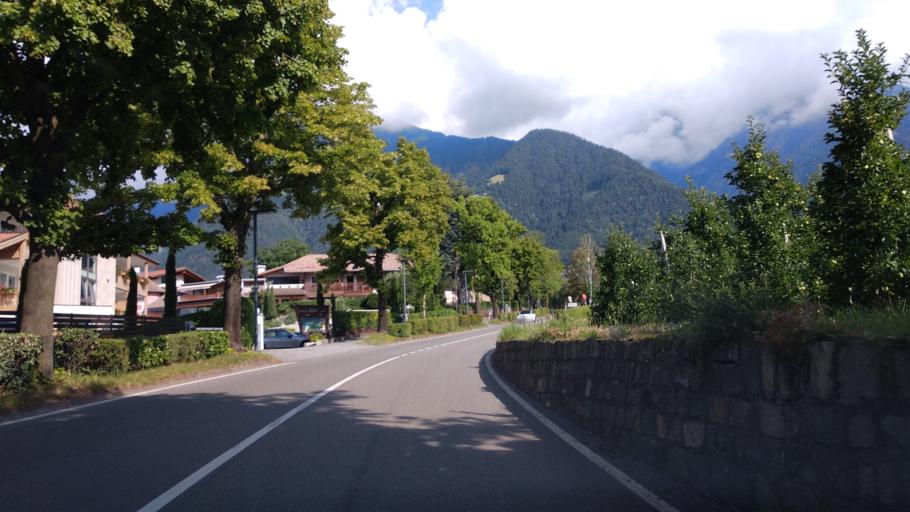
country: IT
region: Trentino-Alto Adige
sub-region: Bolzano
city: Tirolo
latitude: 46.6831
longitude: 11.1611
